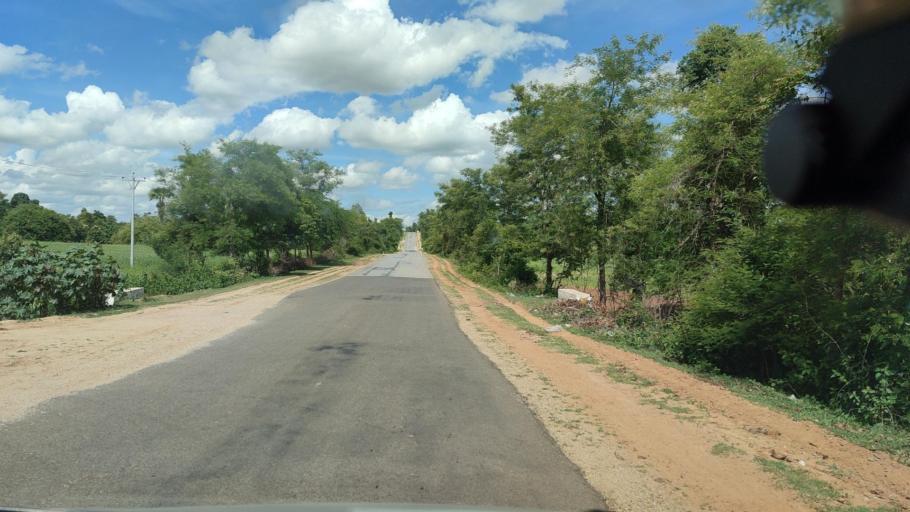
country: MM
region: Magway
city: Magway
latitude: 20.1997
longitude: 95.2327
